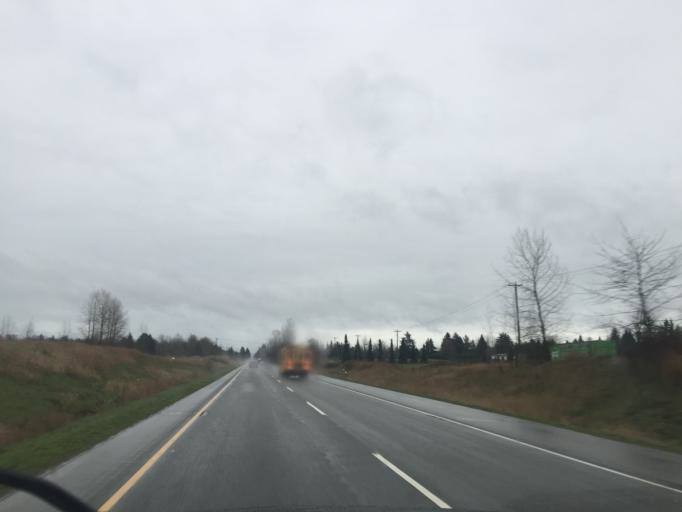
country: CA
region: British Columbia
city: Aldergrove
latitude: 49.0859
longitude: -122.4534
